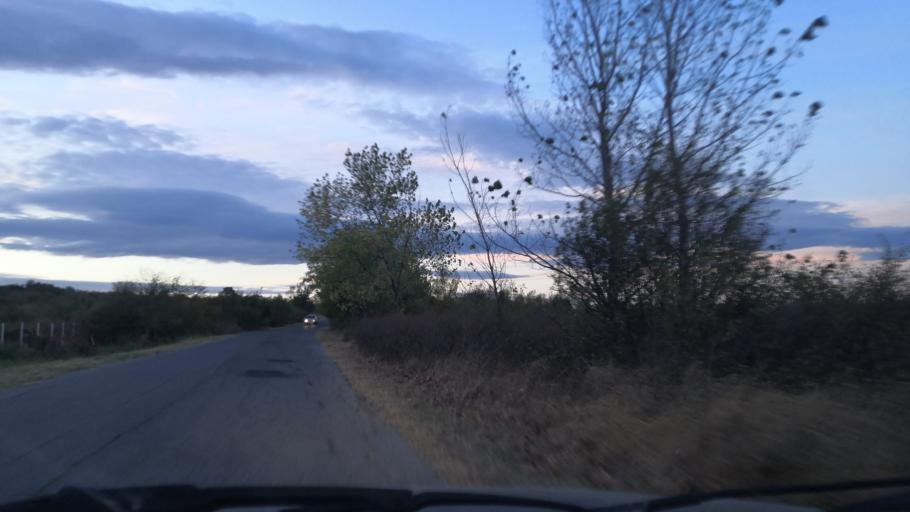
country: RO
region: Mehedinti
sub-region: Comuna Gogosu
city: Balta Verde
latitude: 44.2998
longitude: 22.5533
